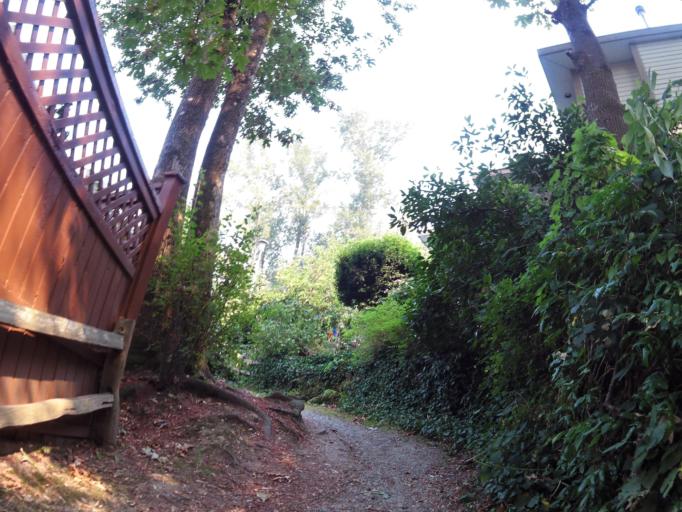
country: CA
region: British Columbia
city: Delta
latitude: 49.1501
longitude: -122.9340
